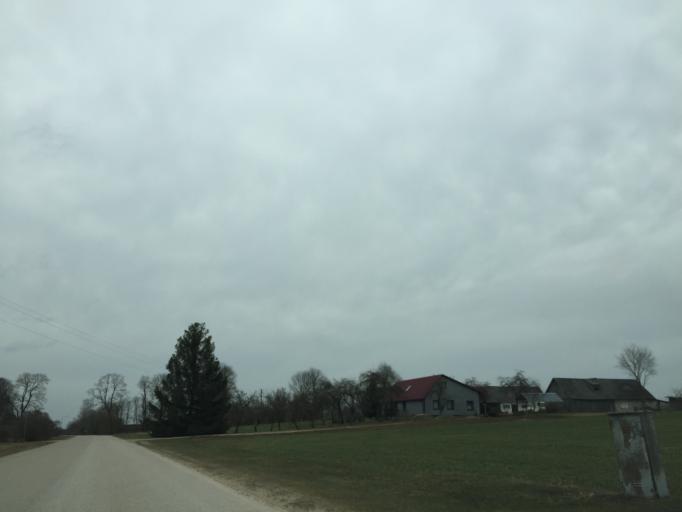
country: LV
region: Livani
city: Livani
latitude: 56.3293
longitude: 26.1596
